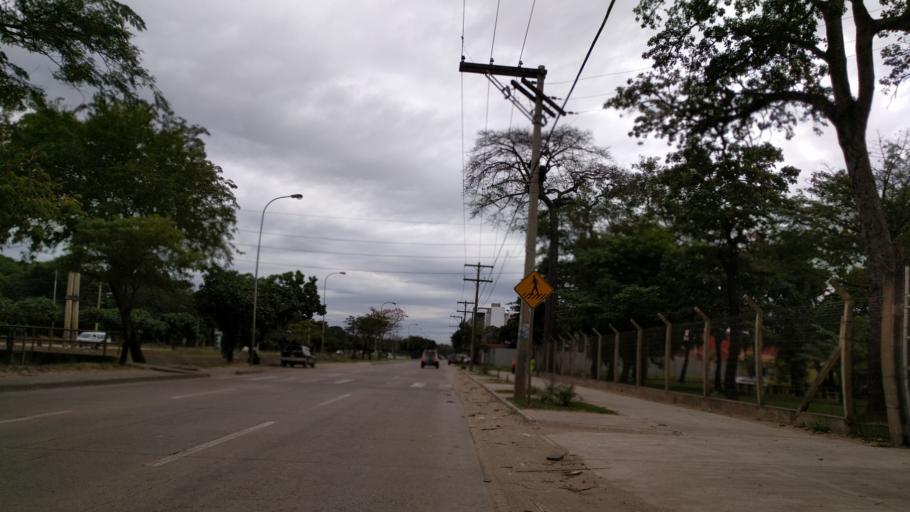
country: BO
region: Santa Cruz
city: Santa Cruz de la Sierra
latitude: -17.7838
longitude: -63.2164
